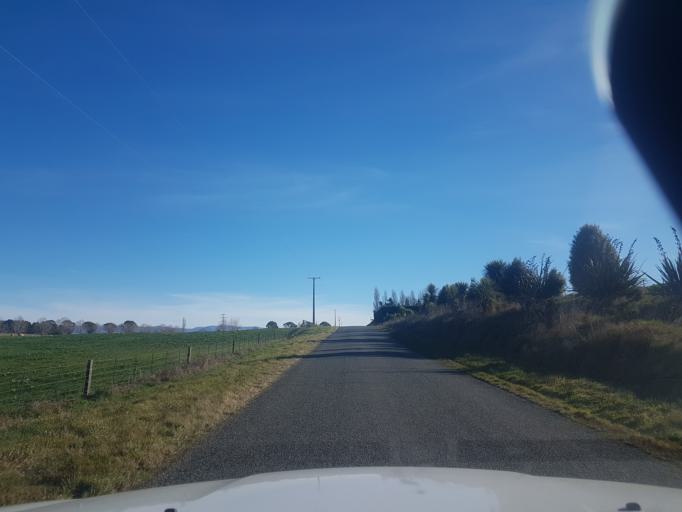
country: NZ
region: Canterbury
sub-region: Timaru District
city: Pleasant Point
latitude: -44.2516
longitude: 171.0571
